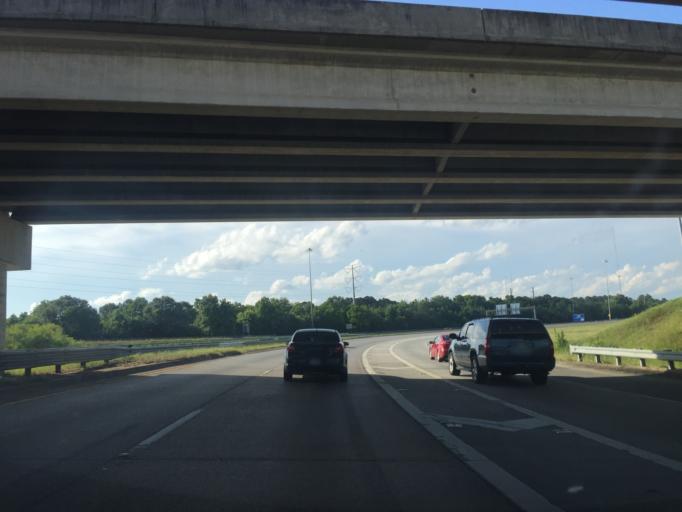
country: US
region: Georgia
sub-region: Chatham County
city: Savannah
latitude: 32.0417
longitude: -81.1463
